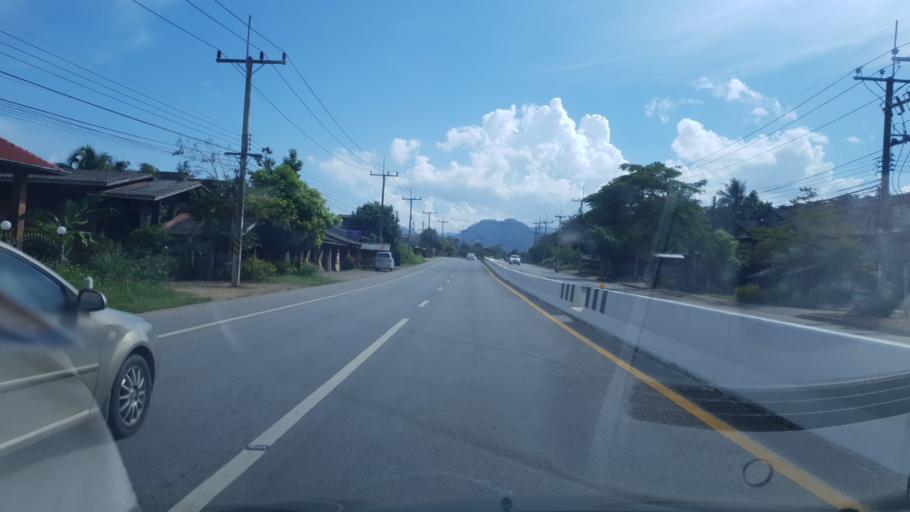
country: TH
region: Lampang
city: Wang Nuea
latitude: 19.1520
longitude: 99.5004
